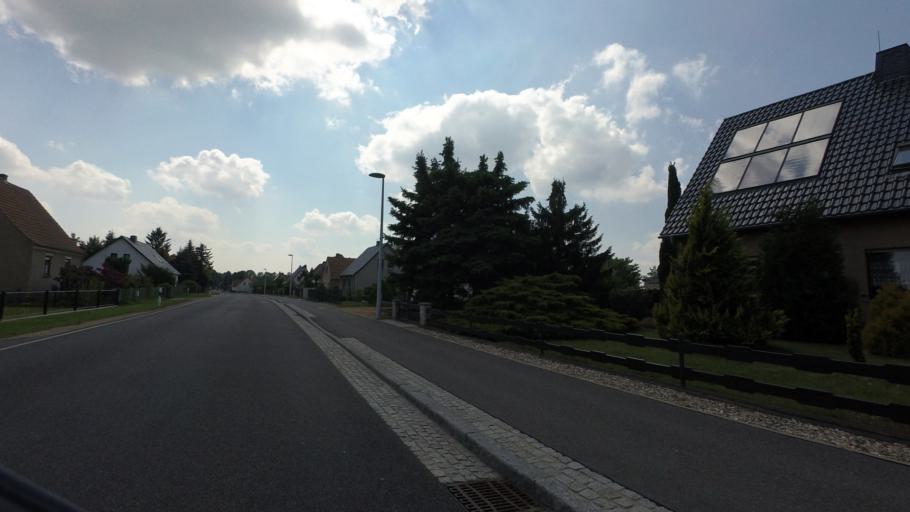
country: DE
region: Saxony
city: Mucka
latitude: 51.3012
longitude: 14.6681
